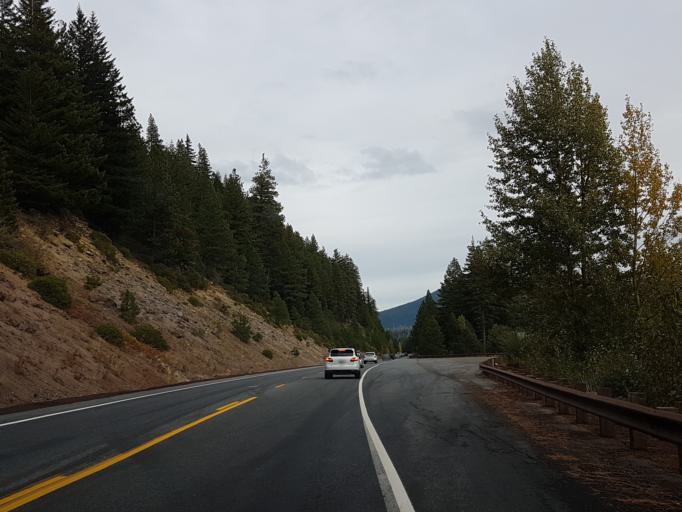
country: US
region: Oregon
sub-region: Deschutes County
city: Sisters
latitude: 44.4189
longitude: -121.7745
